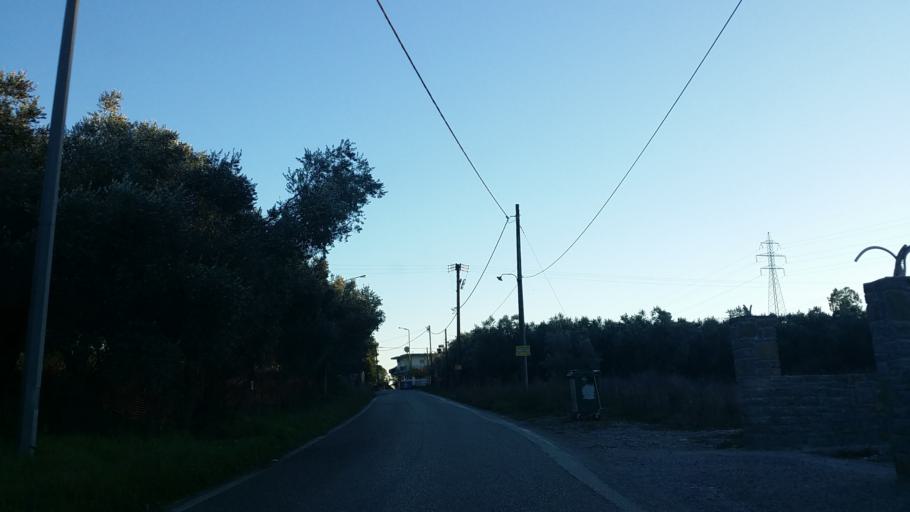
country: GR
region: West Greece
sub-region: Nomos Aitolias kai Akarnanias
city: Neapolis
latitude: 38.6951
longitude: 21.3532
